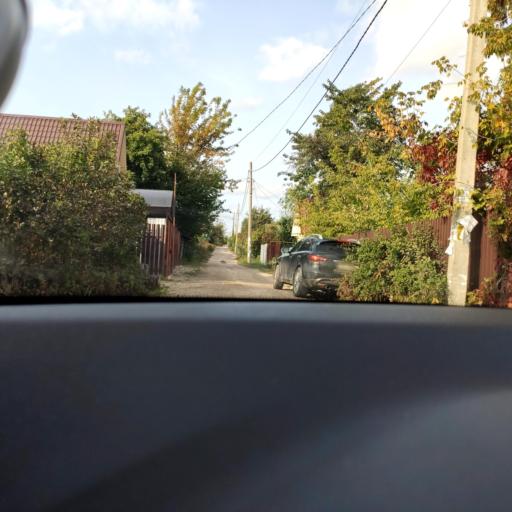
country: RU
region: Samara
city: Petra-Dubrava
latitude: 53.2783
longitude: 50.2963
